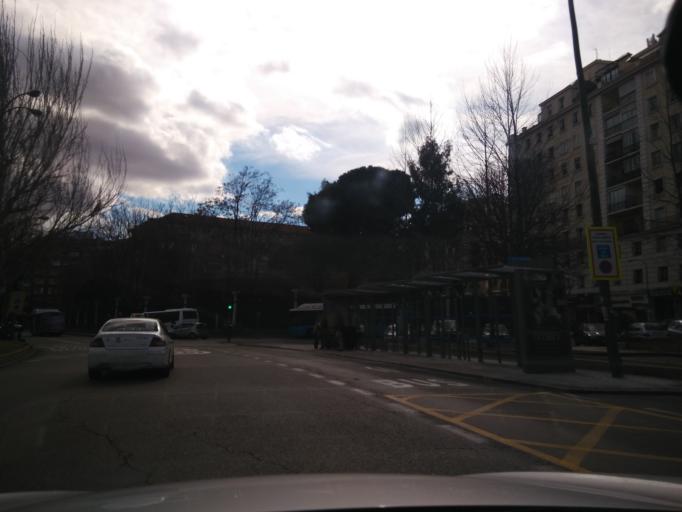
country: ES
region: Madrid
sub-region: Provincia de Madrid
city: Chamberi
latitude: 40.4413
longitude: -3.6921
